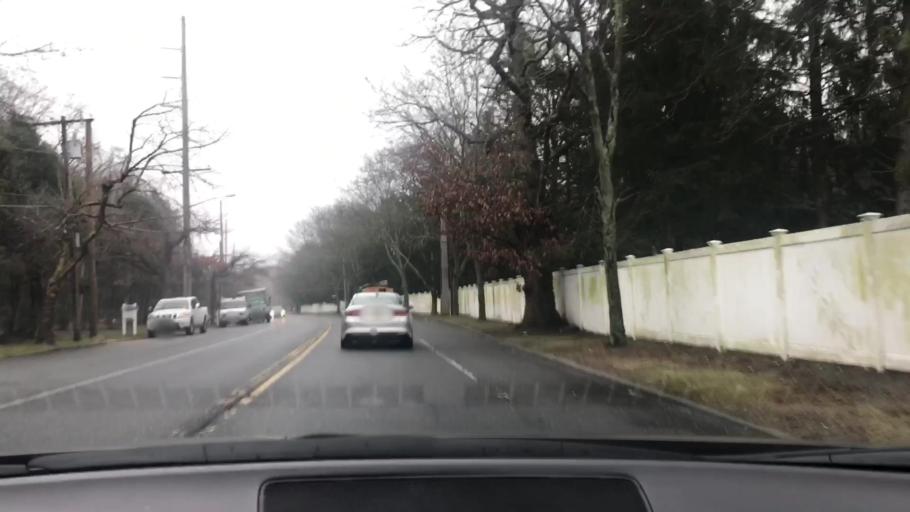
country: US
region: New York
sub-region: Suffolk County
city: South Huntington
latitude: 40.8164
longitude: -73.3777
